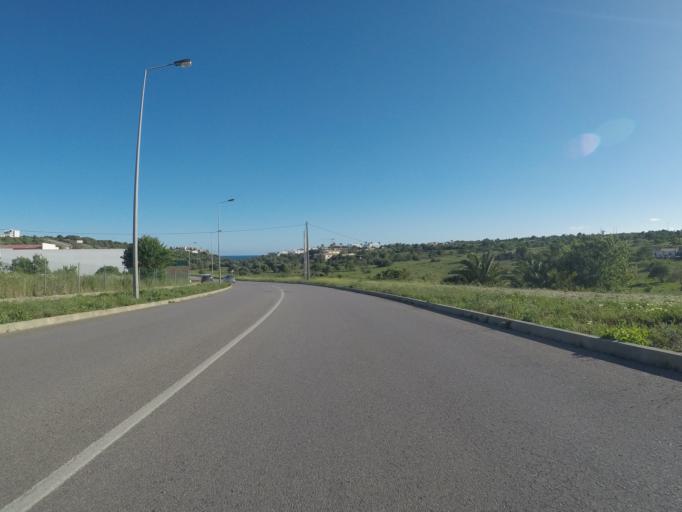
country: PT
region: Faro
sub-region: Lagos
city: Lagos
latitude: 37.0979
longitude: -8.6886
